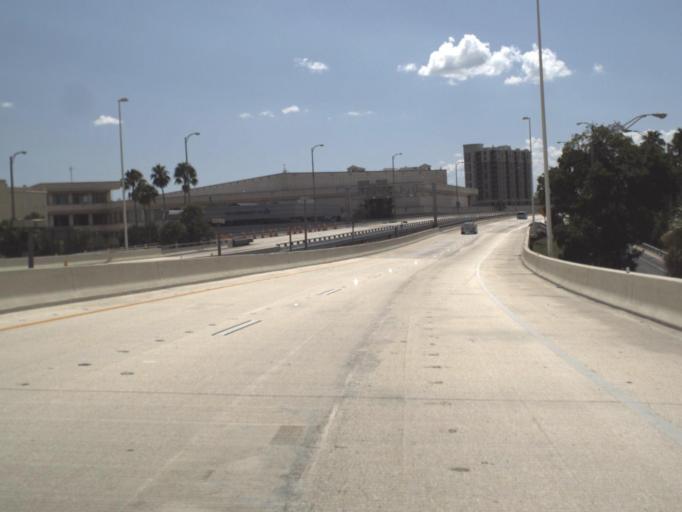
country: US
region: Florida
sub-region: Hillsborough County
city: Tampa
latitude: 27.9445
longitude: -82.4539
